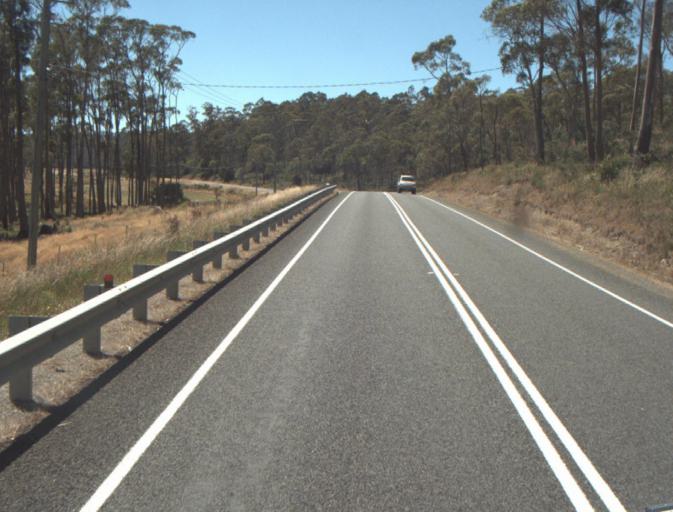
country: AU
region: Tasmania
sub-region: Launceston
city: Newstead
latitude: -41.3686
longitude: 147.3252
